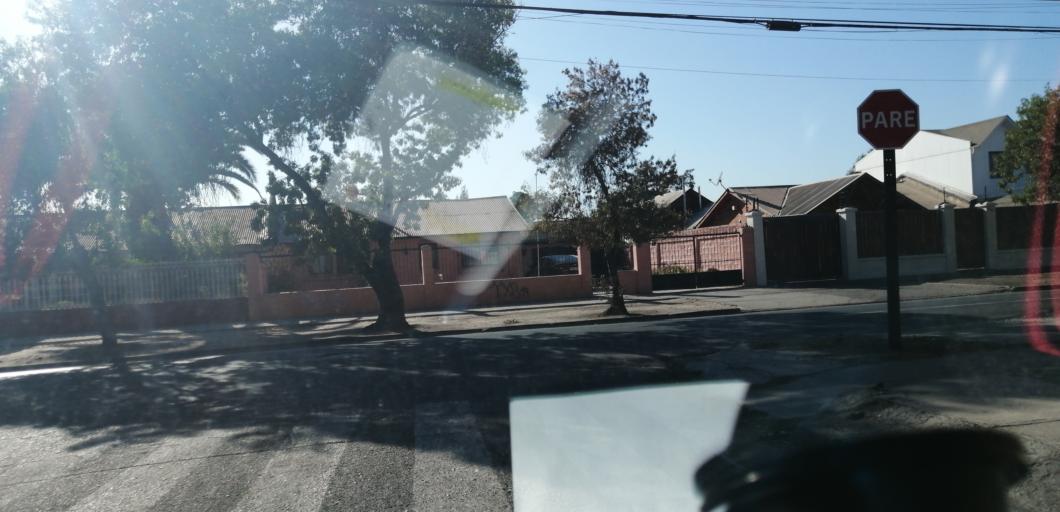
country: CL
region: Santiago Metropolitan
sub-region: Provincia de Santiago
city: Lo Prado
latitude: -33.4367
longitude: -70.7602
